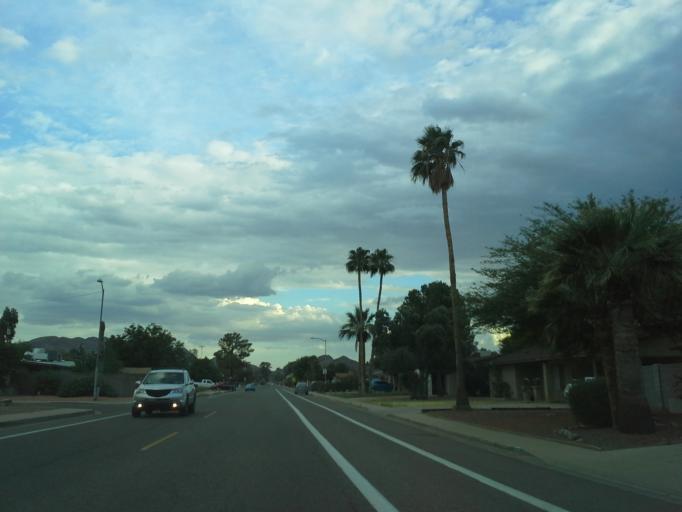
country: US
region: Arizona
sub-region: Maricopa County
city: Paradise Valley
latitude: 33.5957
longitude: -112.0045
